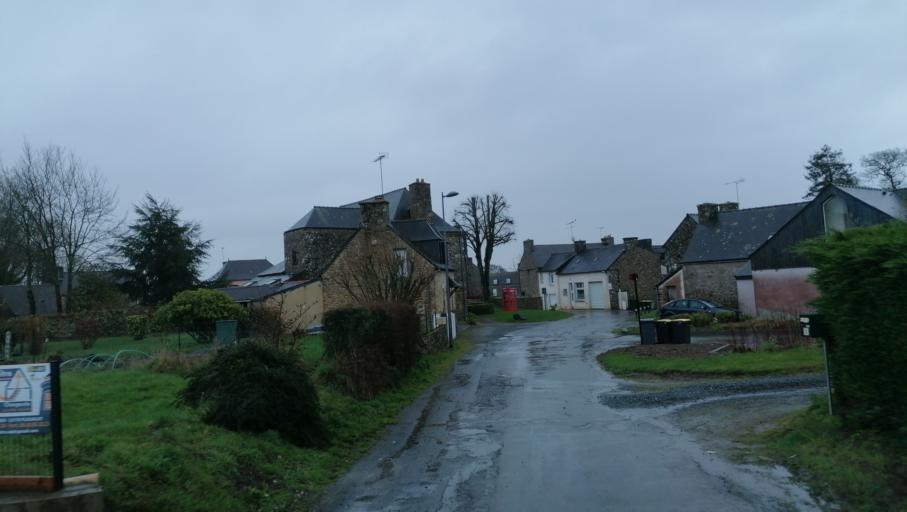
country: FR
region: Brittany
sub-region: Departement des Cotes-d'Armor
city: Plouagat
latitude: 48.4835
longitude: -2.9611
